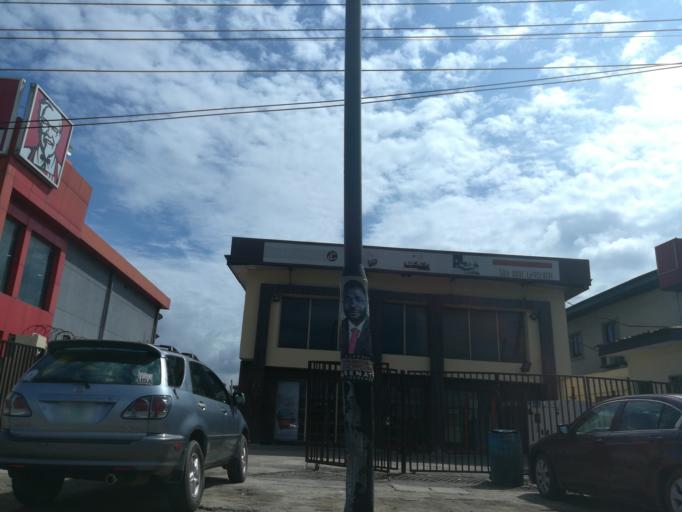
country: NG
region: Lagos
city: Somolu
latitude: 6.5492
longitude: 3.3782
